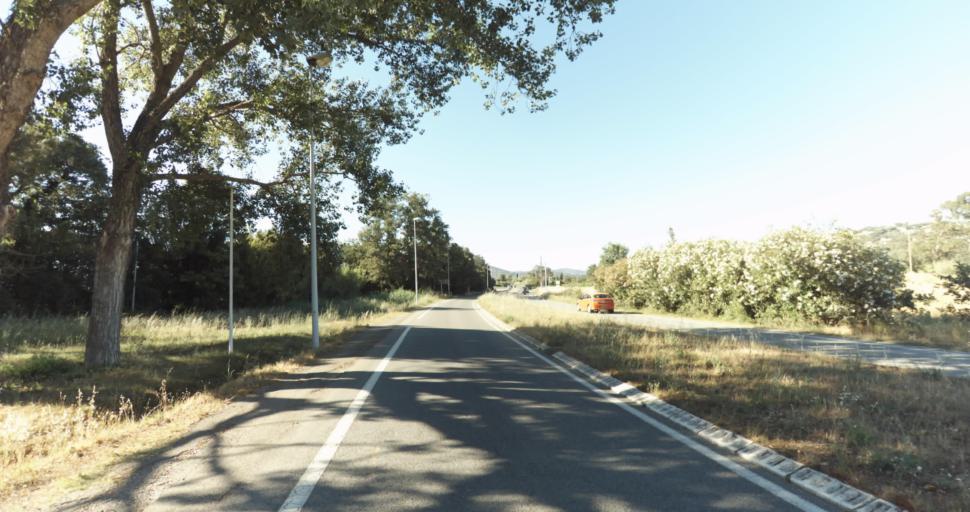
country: FR
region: Provence-Alpes-Cote d'Azur
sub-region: Departement du Var
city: Gassin
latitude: 43.2509
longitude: 6.5920
